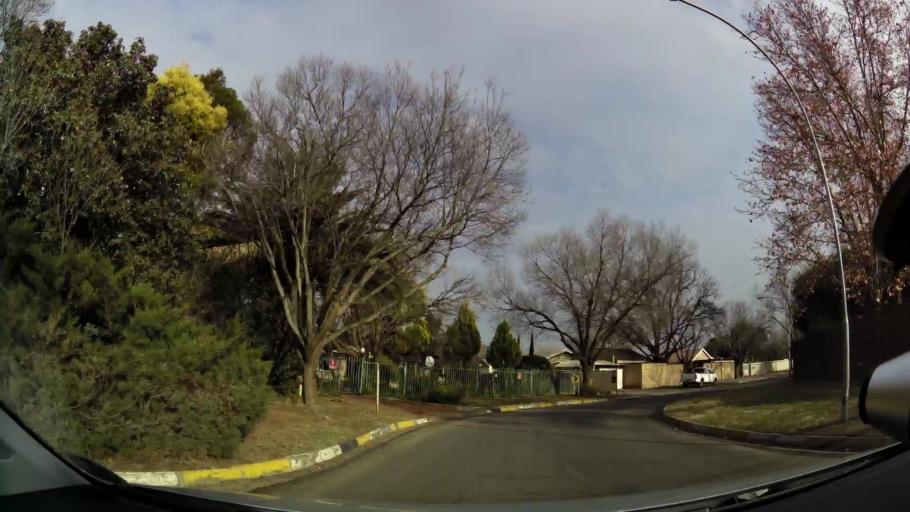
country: ZA
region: Orange Free State
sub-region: Mangaung Metropolitan Municipality
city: Bloemfontein
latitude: -29.1216
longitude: 26.1771
